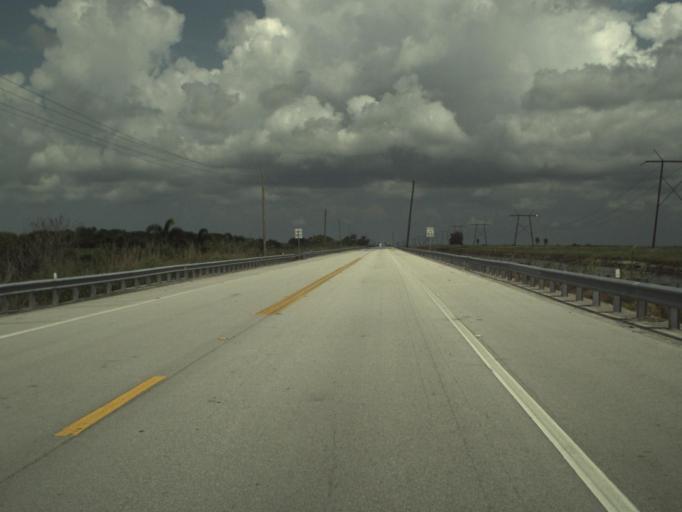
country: US
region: Florida
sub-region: Palm Beach County
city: Pahokee
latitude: 26.7540
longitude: -80.4856
